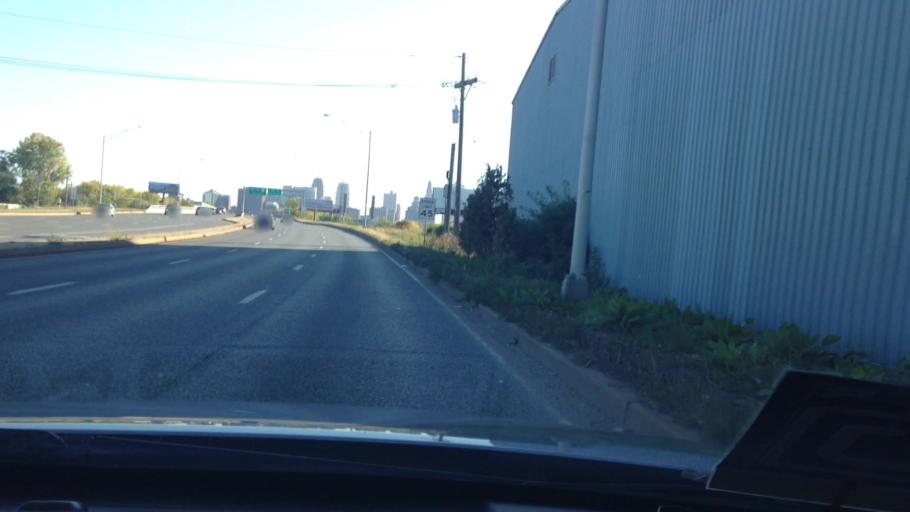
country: US
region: Missouri
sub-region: Clay County
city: North Kansas City
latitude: 39.1263
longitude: -94.5808
